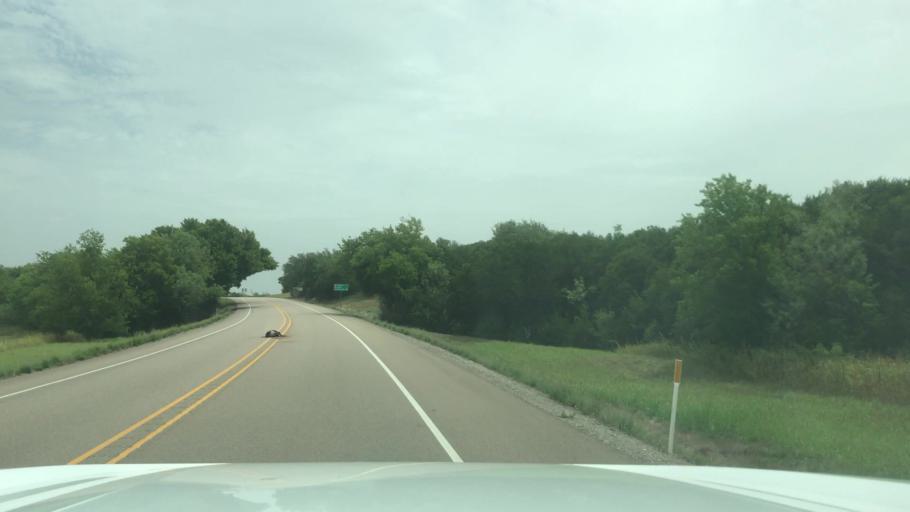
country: US
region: Texas
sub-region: Hamilton County
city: Hico
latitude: 31.9772
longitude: -97.8810
